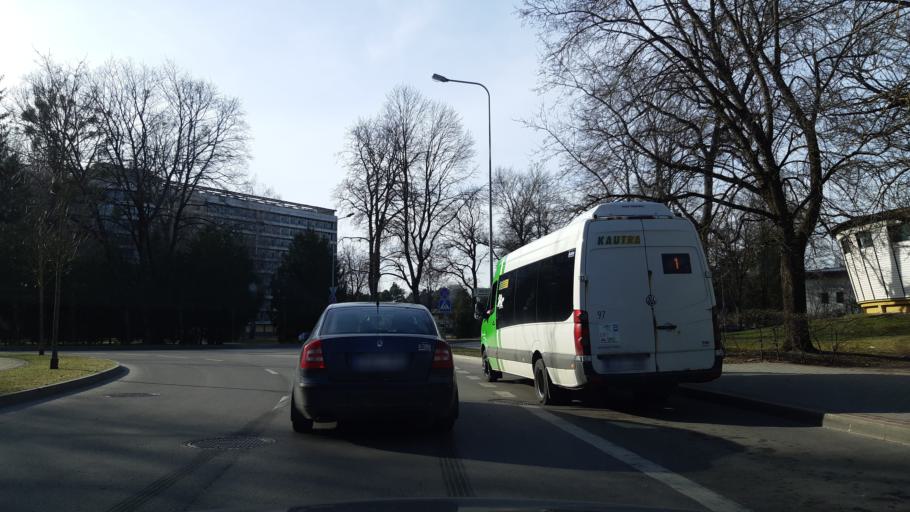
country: LT
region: Alytaus apskritis
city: Druskininkai
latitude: 54.0216
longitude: 23.9715
